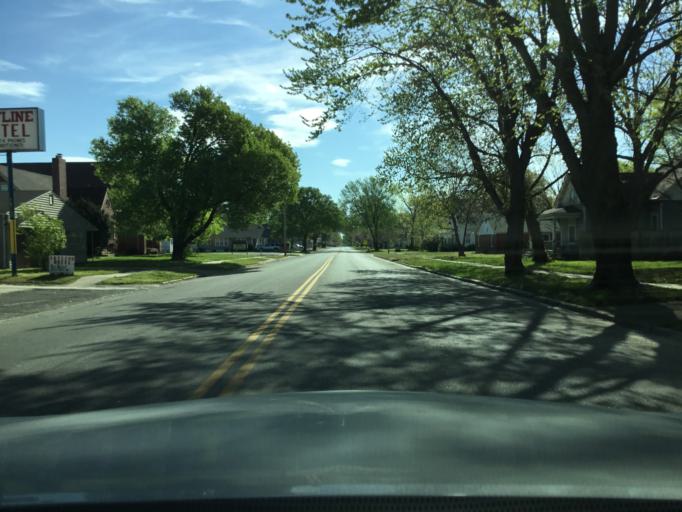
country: US
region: Kansas
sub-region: Neosho County
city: Chanute
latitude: 37.6820
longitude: -95.4696
